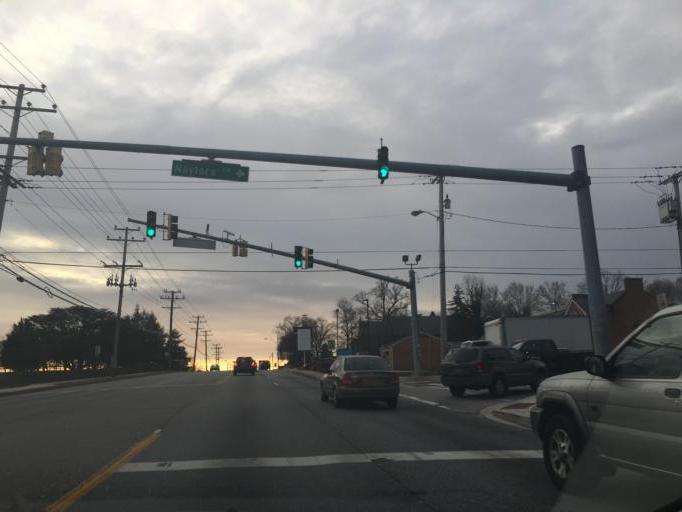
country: US
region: Maryland
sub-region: Baltimore County
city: Pikesville
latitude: 39.3802
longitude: -76.7290
